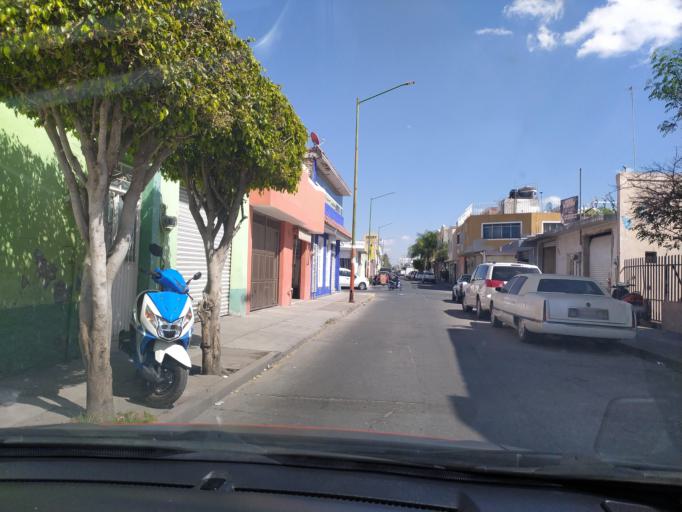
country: LA
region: Oudomxai
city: Muang La
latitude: 21.0240
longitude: 101.8547
